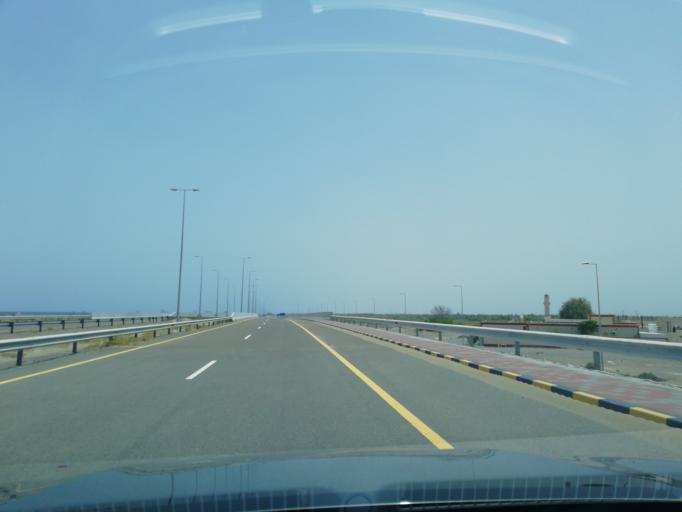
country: OM
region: Al Batinah
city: Shinas
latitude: 24.8707
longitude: 56.4079
